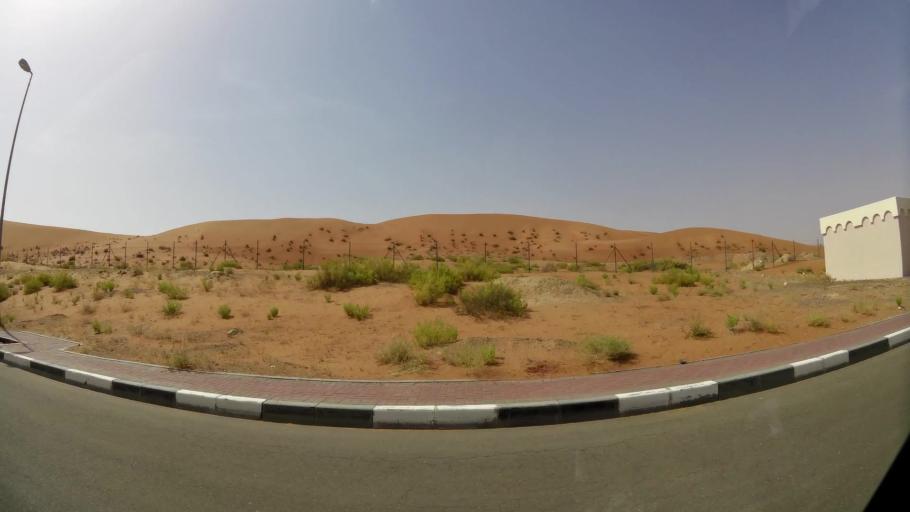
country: AE
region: Abu Dhabi
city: Al Ain
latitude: 24.1543
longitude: 55.6783
